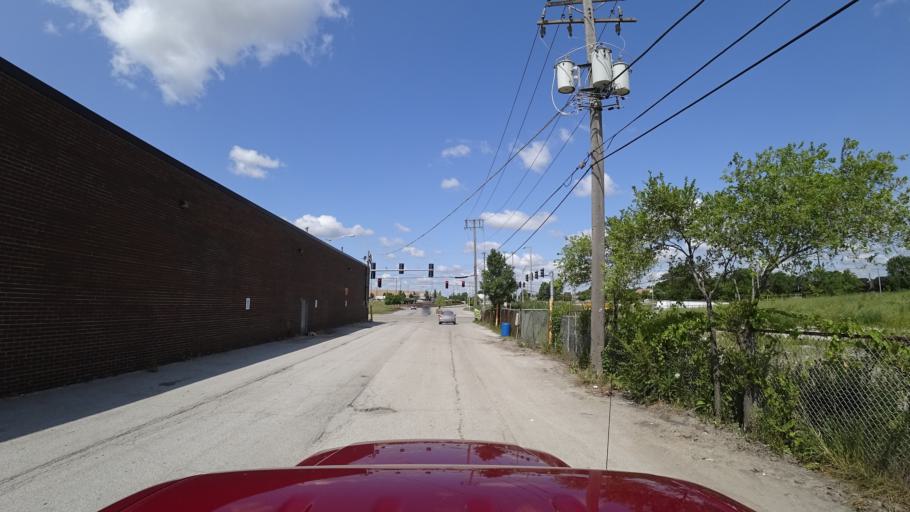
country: US
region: Illinois
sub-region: Cook County
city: Cicero
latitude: 41.8319
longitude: -87.7429
